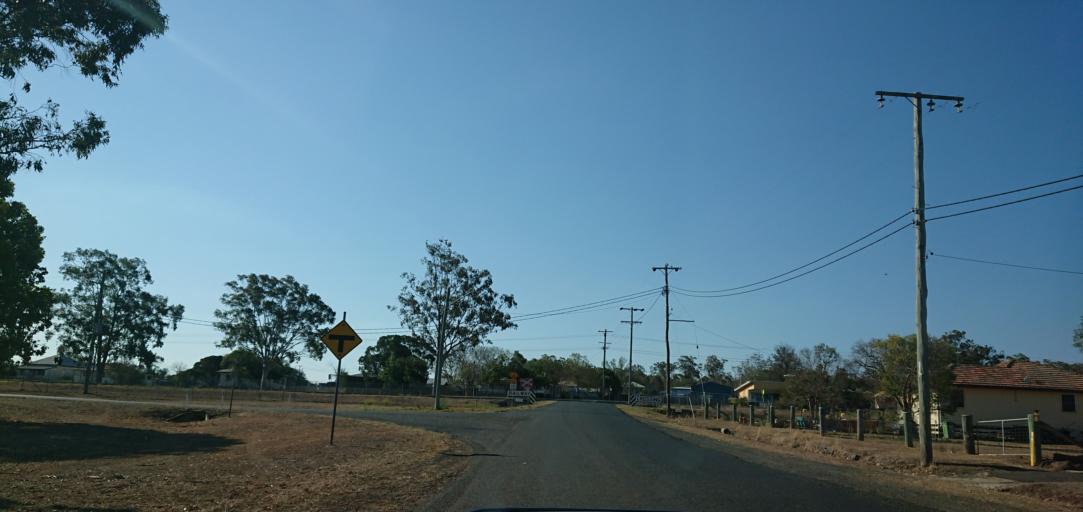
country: AU
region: Queensland
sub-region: Toowoomba
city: Westbrook
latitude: -27.6796
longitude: 151.7130
